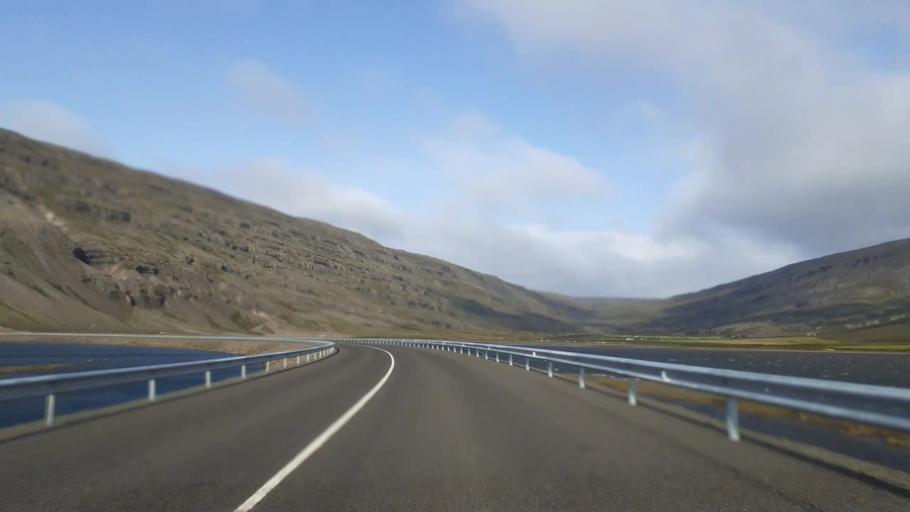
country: IS
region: East
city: Reydarfjoerdur
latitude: 64.7905
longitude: -14.4791
